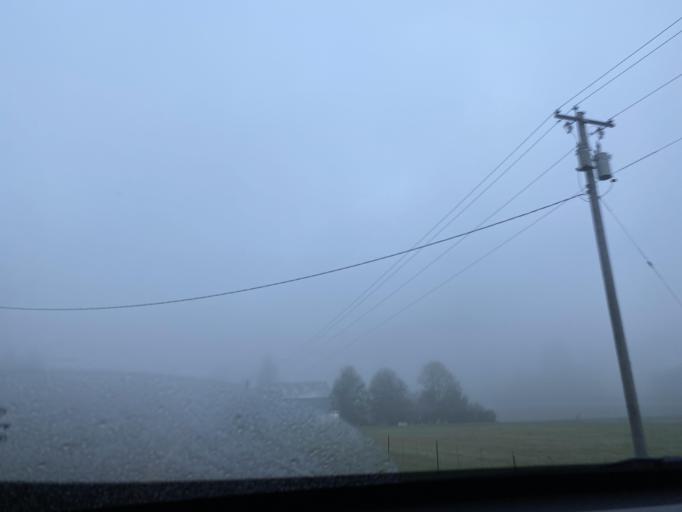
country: US
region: Washington
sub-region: Clallam County
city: Forks
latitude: 47.9357
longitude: -124.3983
